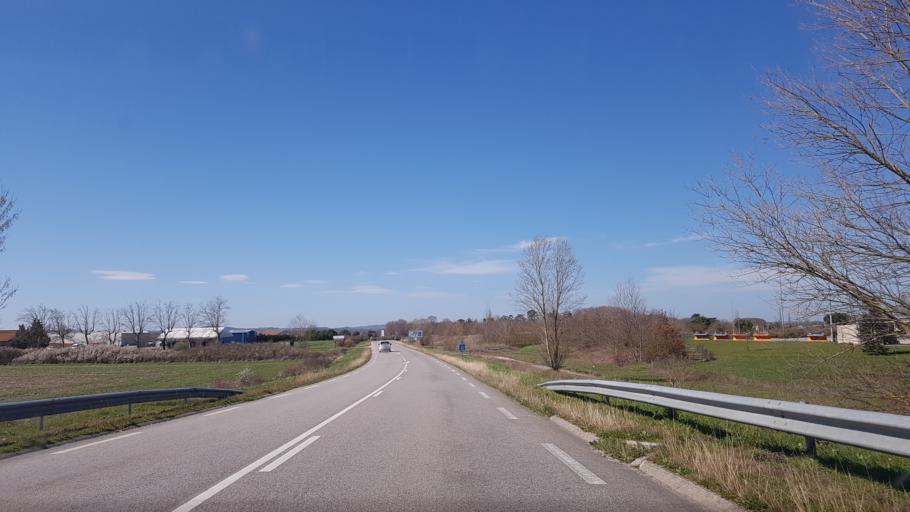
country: FR
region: Midi-Pyrenees
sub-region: Departement de l'Ariege
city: Mazeres
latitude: 43.2330
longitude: 1.6384
